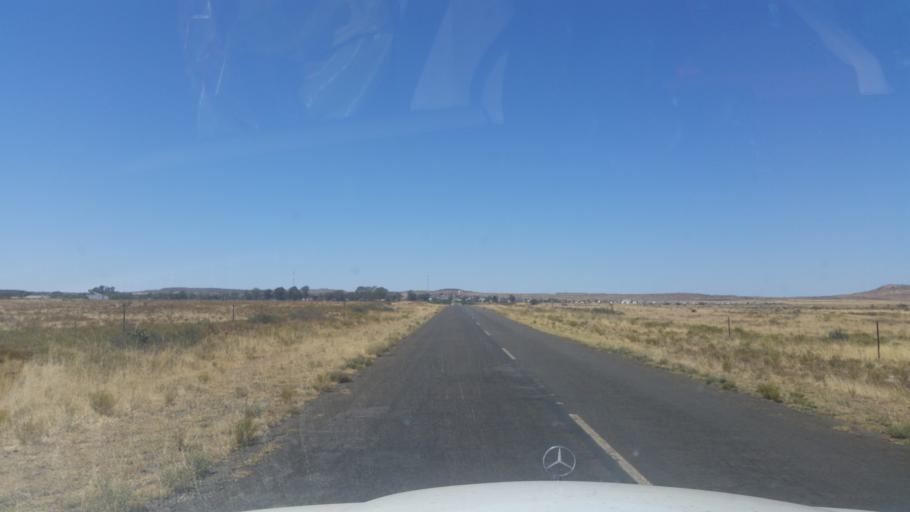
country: ZA
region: Eastern Cape
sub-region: Joe Gqabi District Municipality
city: Burgersdorp
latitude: -30.7657
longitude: 25.7876
